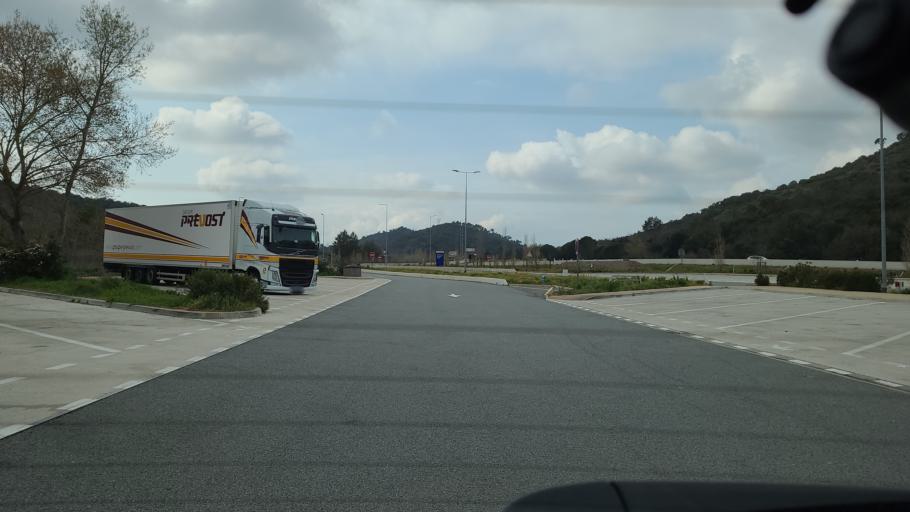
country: FR
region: Provence-Alpes-Cote d'Azur
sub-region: Departement du Var
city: Bagnols-en-Foret
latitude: 43.5008
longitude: 6.7573
